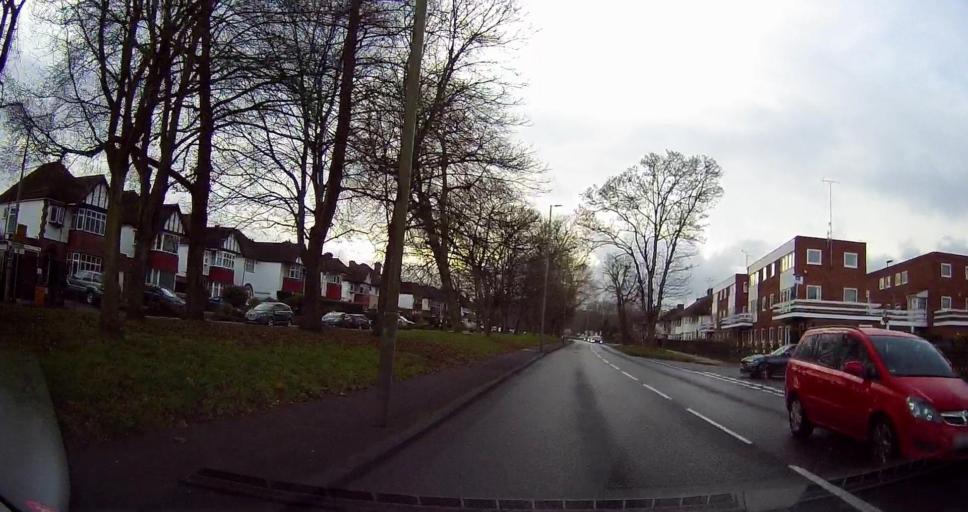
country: GB
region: England
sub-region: Greater London
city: Orpington
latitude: 51.3627
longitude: 0.0911
